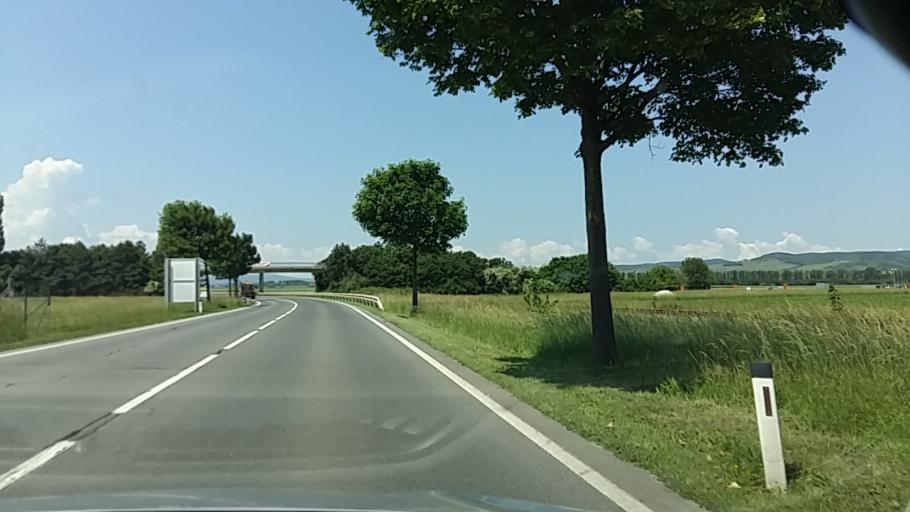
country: AT
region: Burgenland
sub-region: Politischer Bezirk Oberpullendorf
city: Deutschkreutz
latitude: 47.6025
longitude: 16.6083
